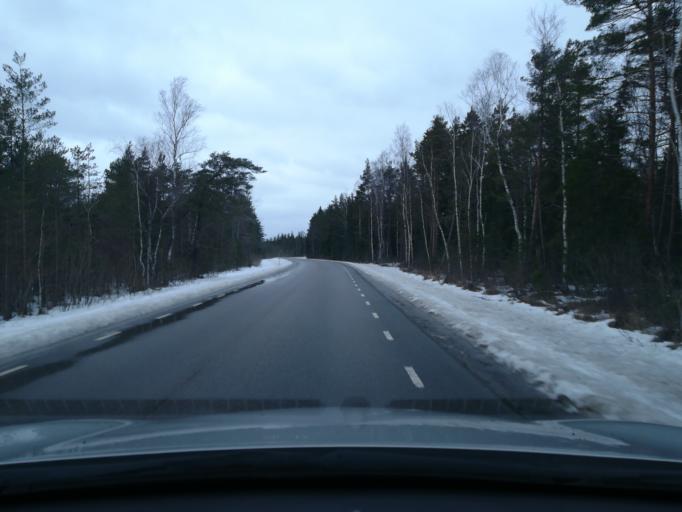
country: EE
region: Harju
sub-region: Nissi vald
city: Riisipere
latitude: 59.1393
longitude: 24.2984
